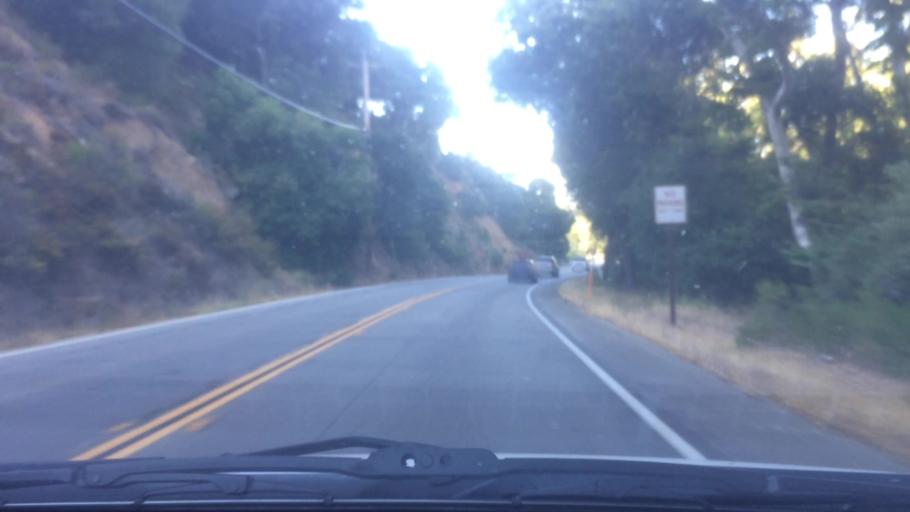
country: US
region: California
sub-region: San Luis Obispo County
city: Atascadero
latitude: 35.4541
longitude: -120.6926
